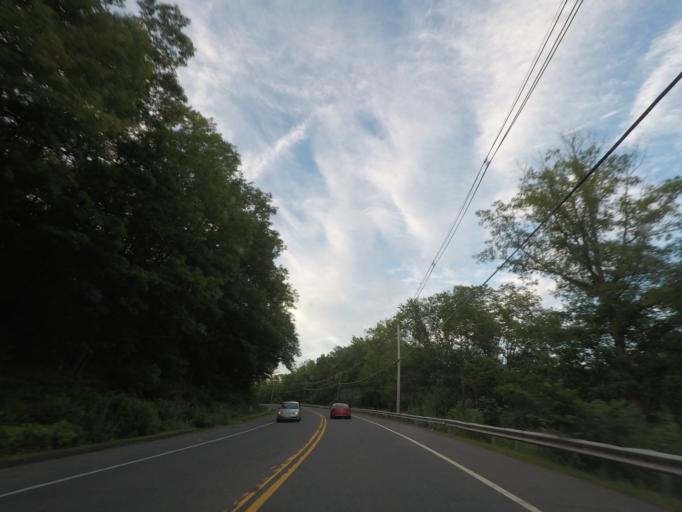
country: US
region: Massachusetts
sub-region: Worcester County
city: Warren
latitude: 42.2137
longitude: -72.2253
